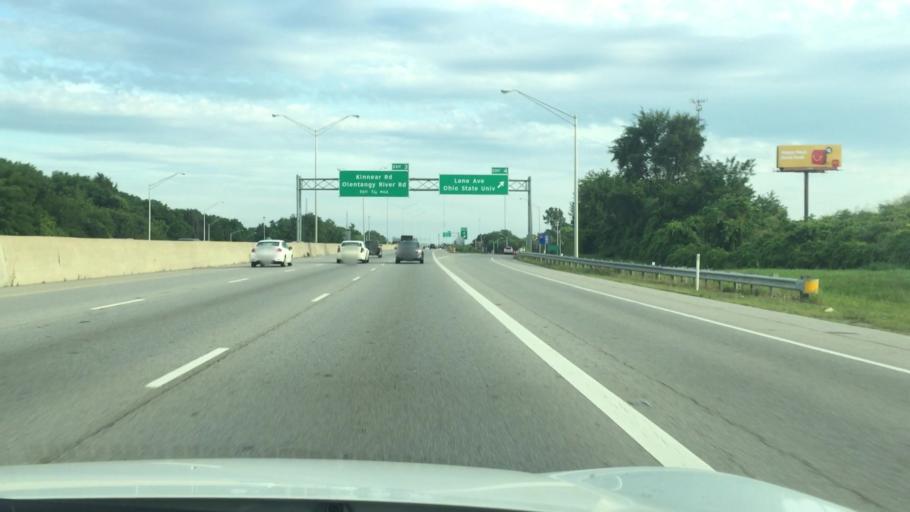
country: US
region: Ohio
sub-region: Franklin County
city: Grandview Heights
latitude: 40.0100
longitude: -83.0317
